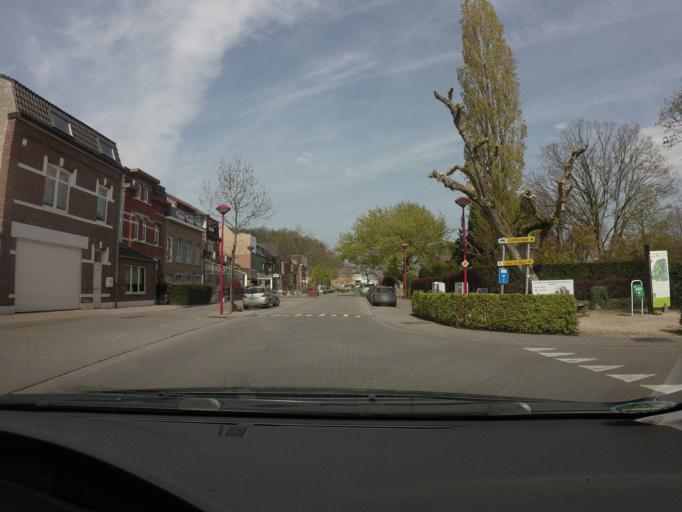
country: NL
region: Limburg
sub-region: Gemeente Maastricht
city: Maastricht
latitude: 50.8145
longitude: 5.6689
